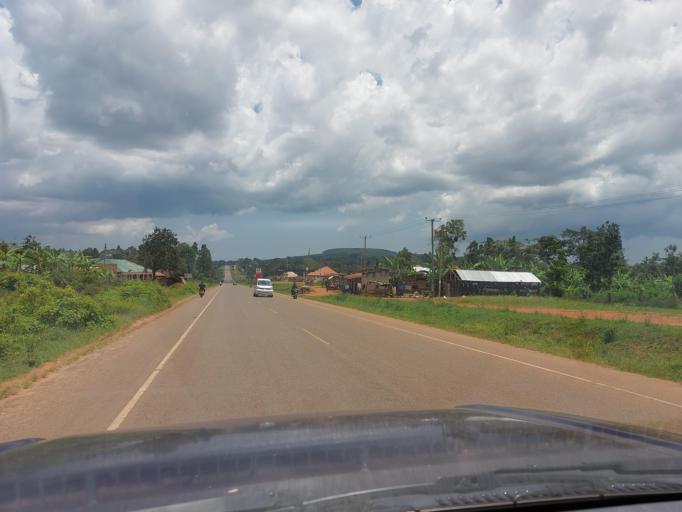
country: UG
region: Central Region
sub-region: Mukono District
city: Mukono
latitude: 0.2955
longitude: 32.7838
